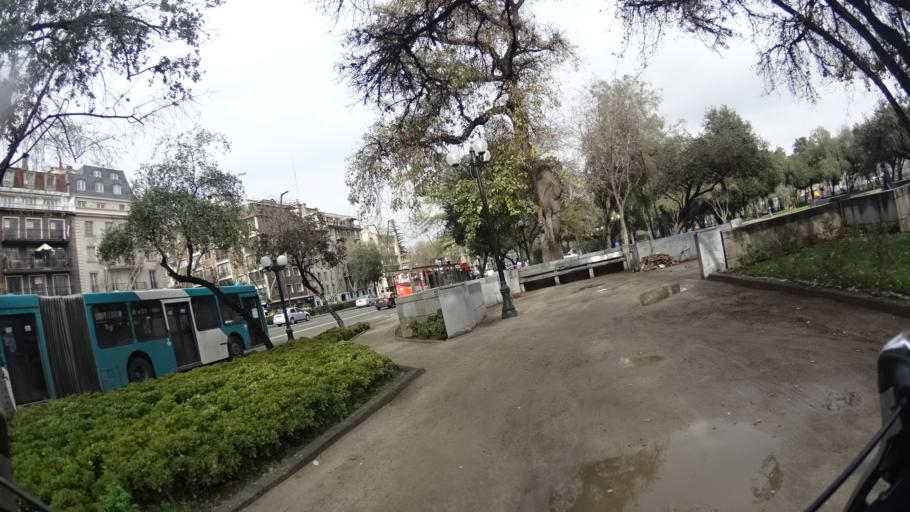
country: CL
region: Santiago Metropolitan
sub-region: Provincia de Santiago
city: Santiago
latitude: -33.4350
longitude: -70.6290
